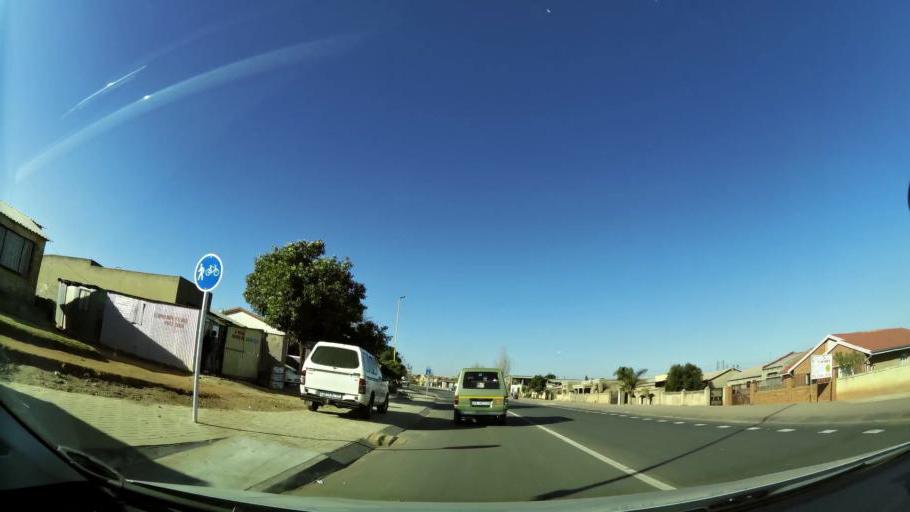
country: ZA
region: Gauteng
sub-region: Ekurhuleni Metropolitan Municipality
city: Tembisa
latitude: -26.0280
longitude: 28.2153
